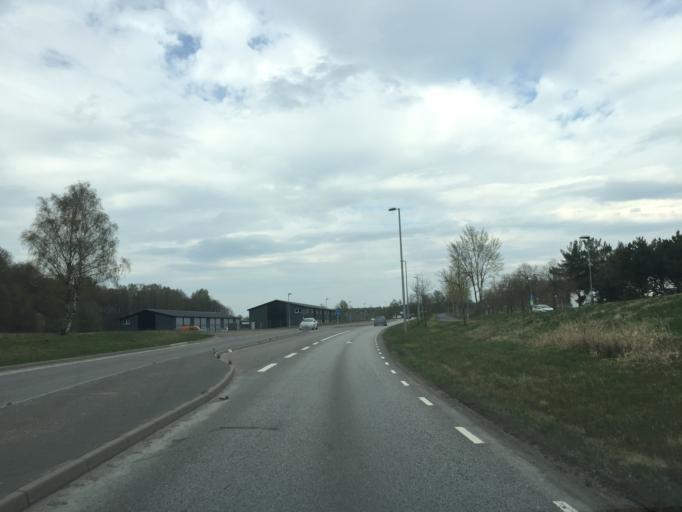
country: SE
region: Vaestra Goetaland
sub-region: Goteborg
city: Loevgaerdet
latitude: 57.8023
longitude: 12.0425
